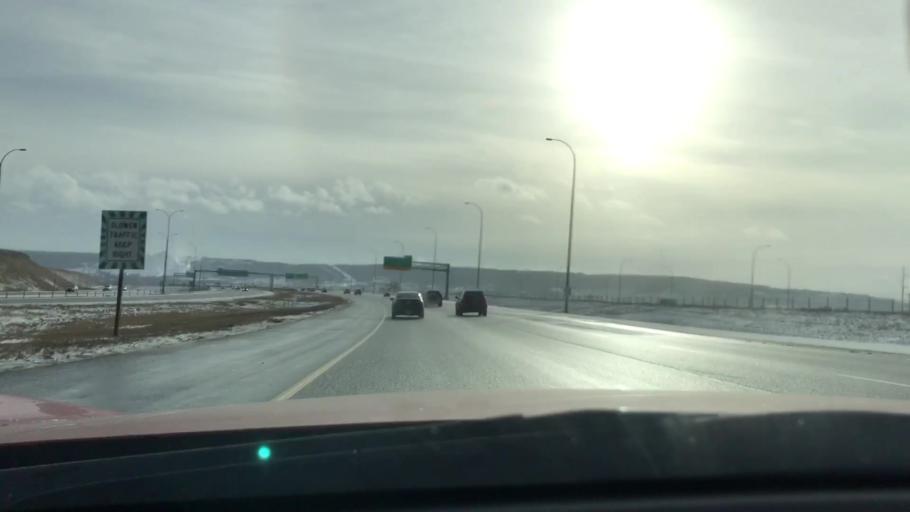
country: CA
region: Alberta
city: Calgary
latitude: 51.1239
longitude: -114.2318
